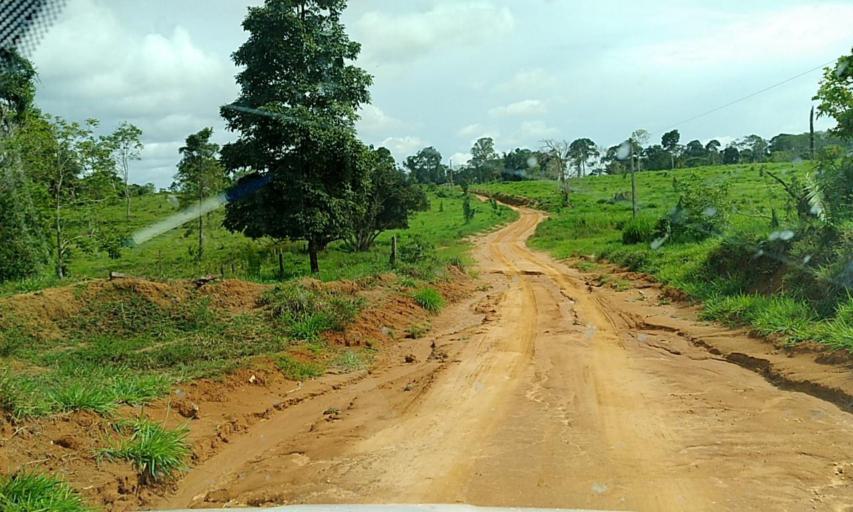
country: BR
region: Para
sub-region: Altamira
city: Altamira
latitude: -3.2284
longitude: -52.7459
